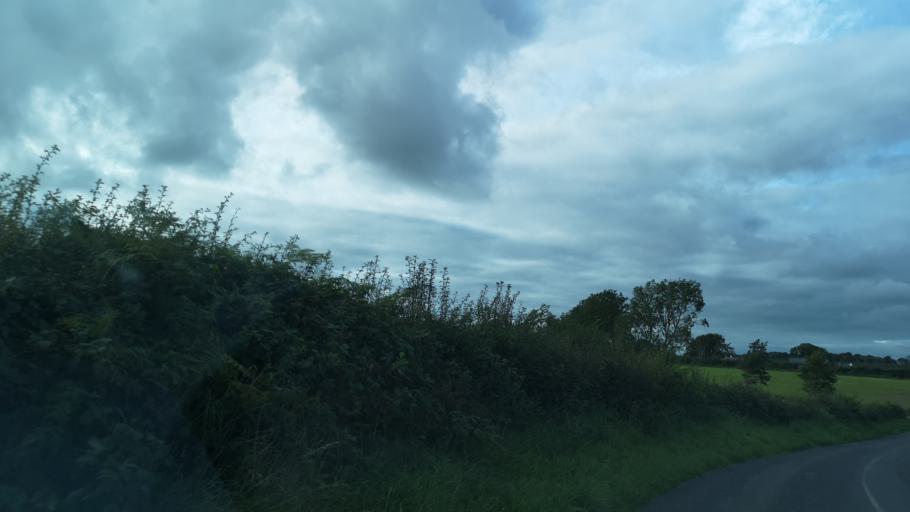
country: IE
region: Connaught
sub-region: County Galway
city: Ballinasloe
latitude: 53.2962
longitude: -8.1032
